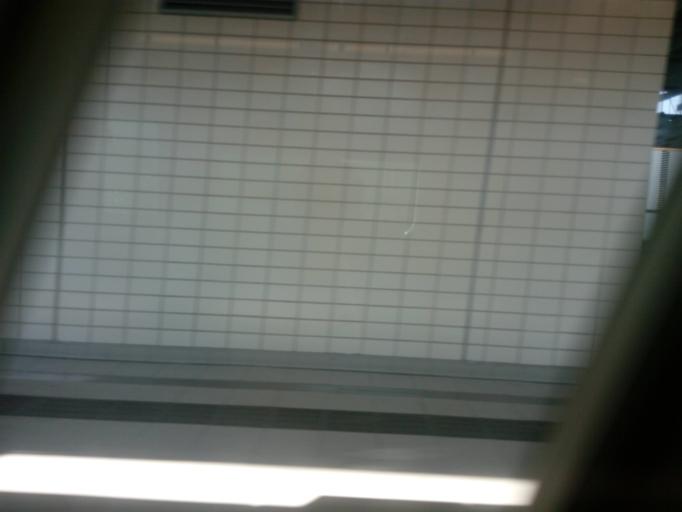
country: HK
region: Sha Tin
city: Sha Tin
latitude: 22.3873
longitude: 114.2079
